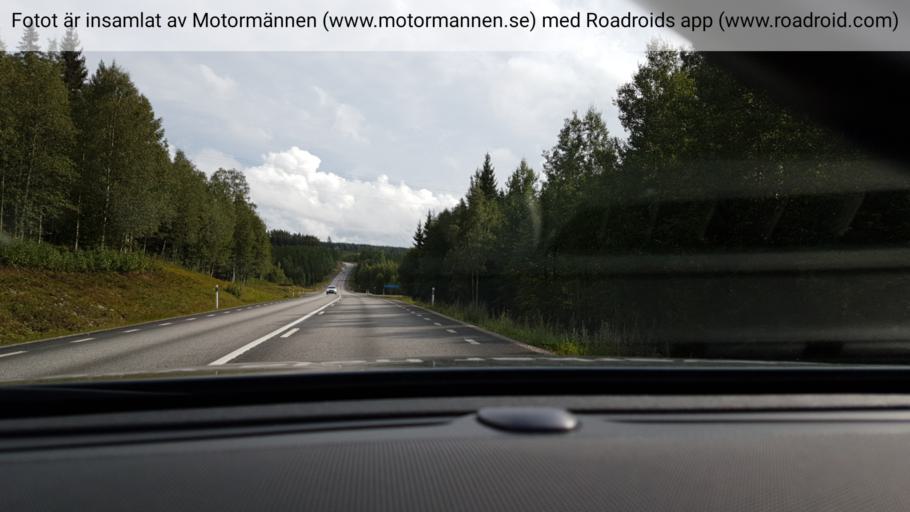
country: SE
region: Dalarna
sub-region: Rattviks Kommun
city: Raettvik
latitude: 60.7954
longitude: 15.2734
